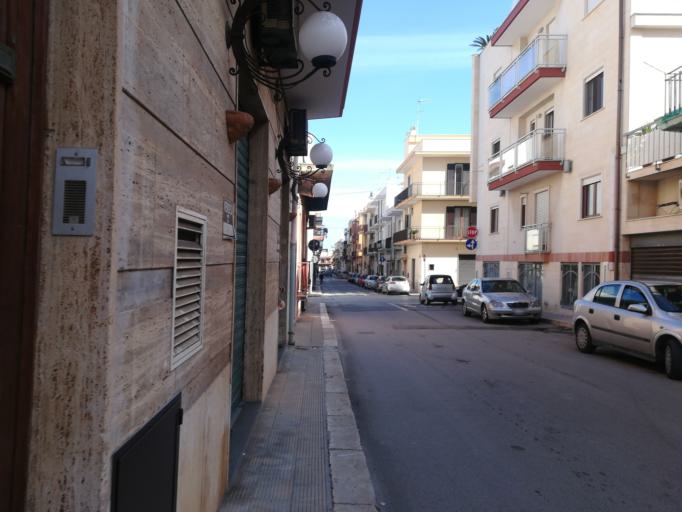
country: IT
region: Apulia
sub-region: Provincia di Bari
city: Polignano a Mare
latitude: 40.9908
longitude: 17.2215
